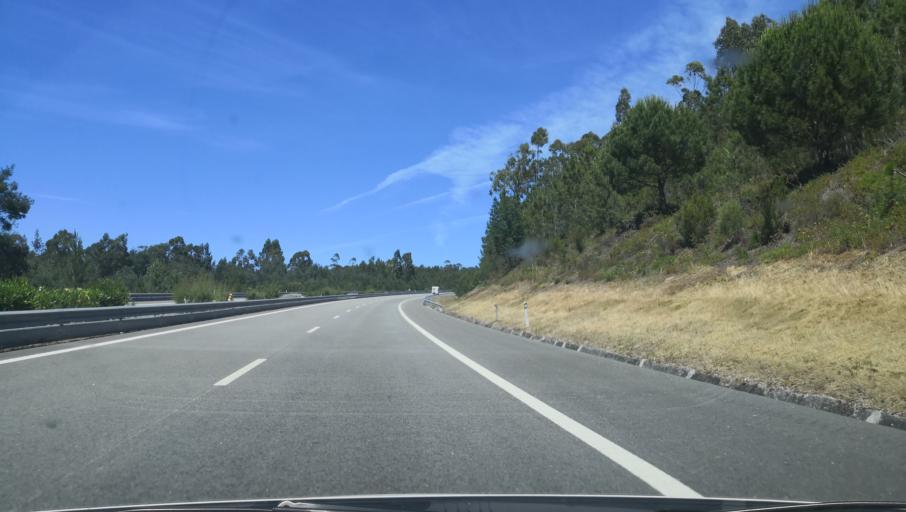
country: PT
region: Coimbra
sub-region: Montemor-O-Velho
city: Arazede
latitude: 40.2448
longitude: -8.6572
